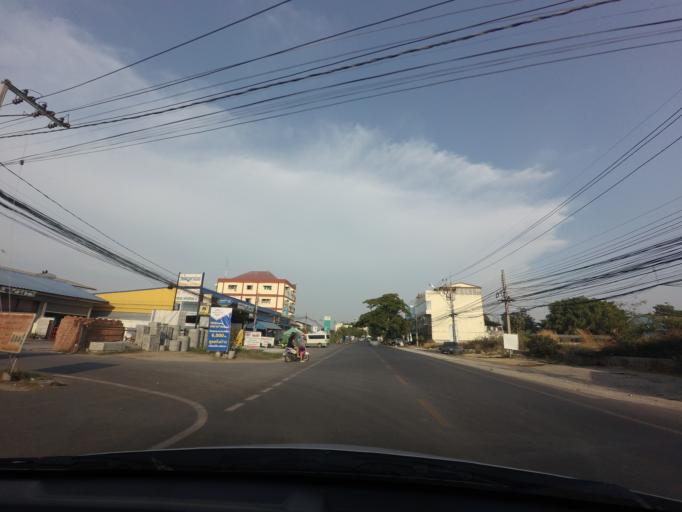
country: TH
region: Bangkok
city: Saphan Sung
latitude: 13.7419
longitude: 100.6804
